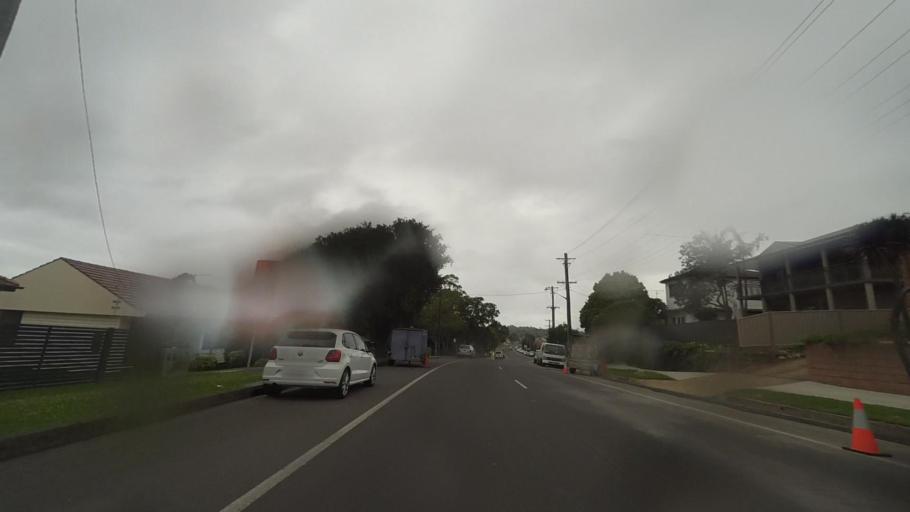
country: AU
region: New South Wales
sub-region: Wollongong
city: Keiraville
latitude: -34.4196
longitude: 150.8621
